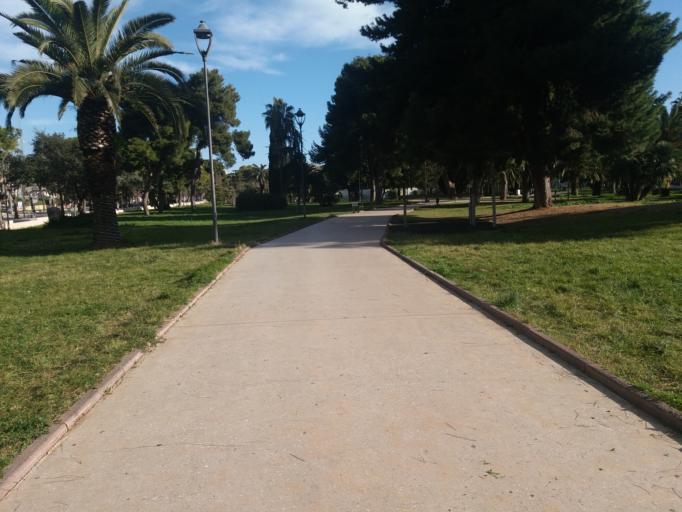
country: IT
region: Apulia
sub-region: Provincia di Barletta - Andria - Trani
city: Andria
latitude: 41.2320
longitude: 16.3058
